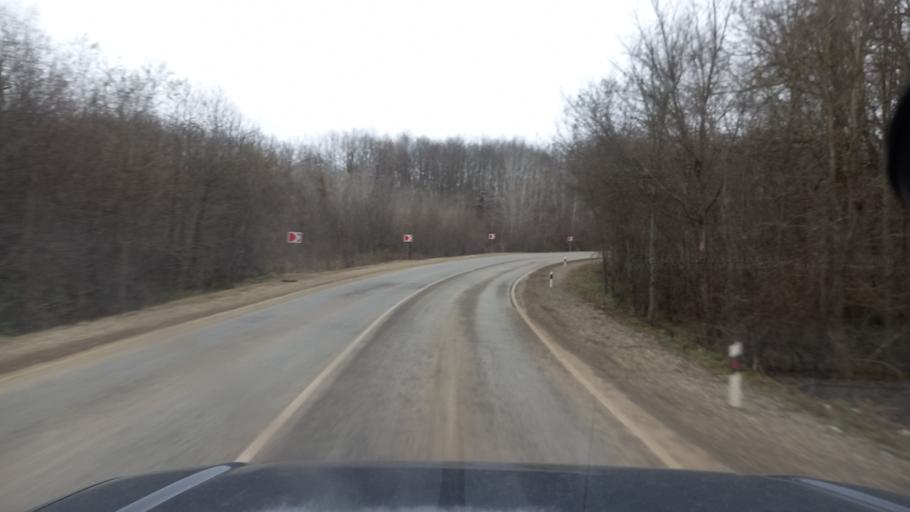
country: RU
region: Krasnodarskiy
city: Saratovskaya
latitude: 44.5430
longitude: 39.2971
